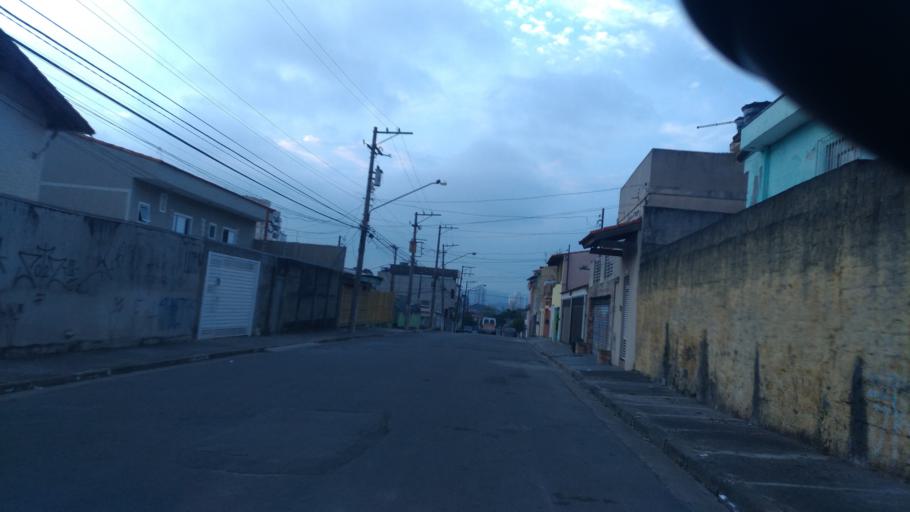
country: BR
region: Sao Paulo
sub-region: Osasco
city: Osasco
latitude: -23.5414
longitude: -46.7990
